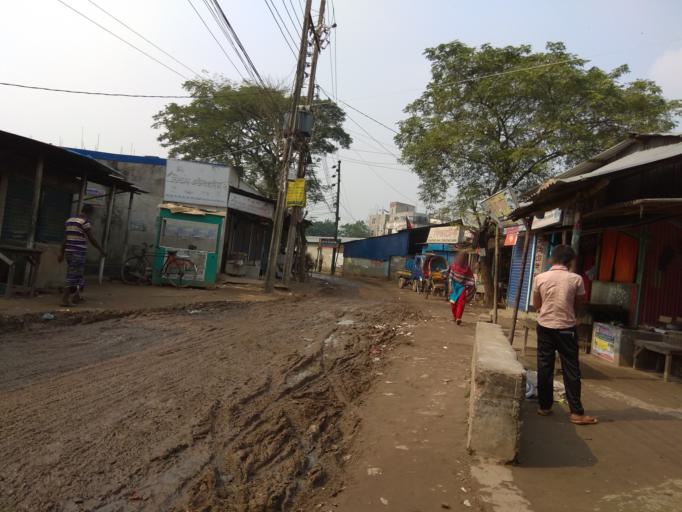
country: BD
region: Dhaka
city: Tungi
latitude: 23.8545
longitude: 90.3822
